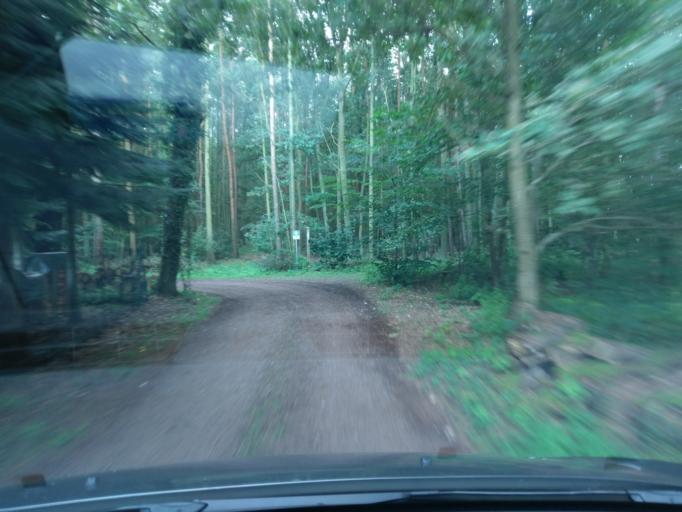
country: DE
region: Brandenburg
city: Gross Kreutz
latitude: 52.3205
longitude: 12.7662
